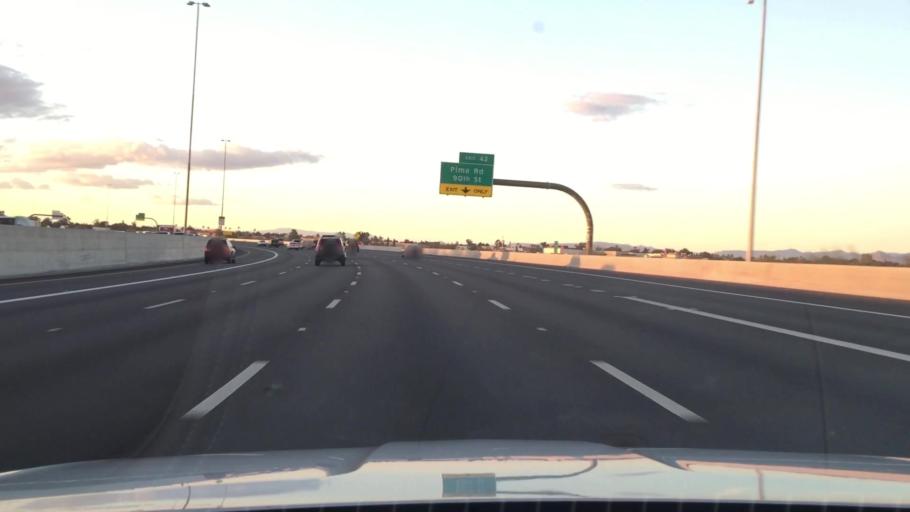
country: US
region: Arizona
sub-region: Maricopa County
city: Scottsdale
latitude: 33.5579
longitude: -111.8783
